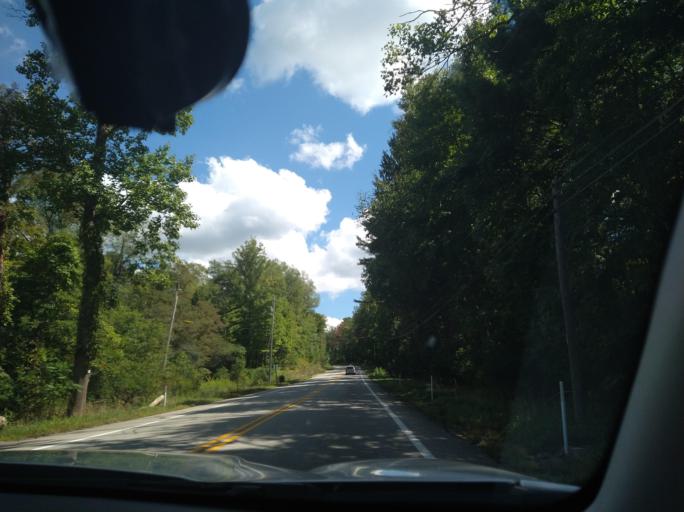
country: US
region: Pennsylvania
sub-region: Fayette County
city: Bear Rocks
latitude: 40.0802
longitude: -79.3259
